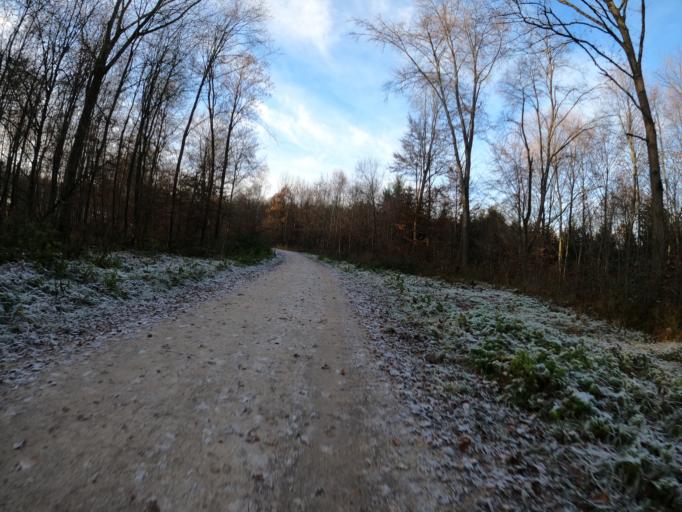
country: DE
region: Baden-Wuerttemberg
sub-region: Regierungsbezirk Stuttgart
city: Albershausen
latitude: 48.6781
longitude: 9.5497
